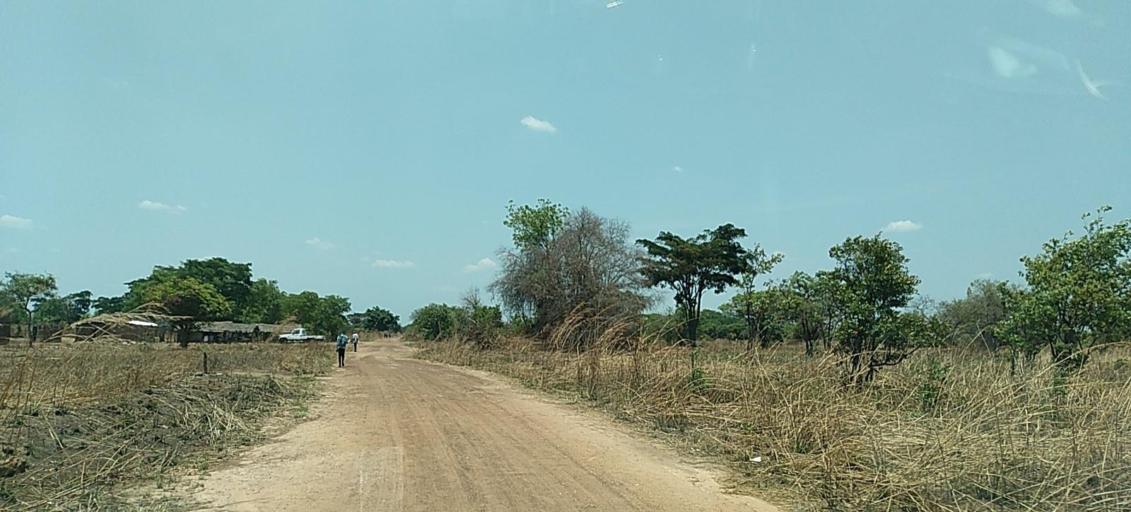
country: ZM
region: Copperbelt
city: Luanshya
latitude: -13.0882
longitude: 28.4060
